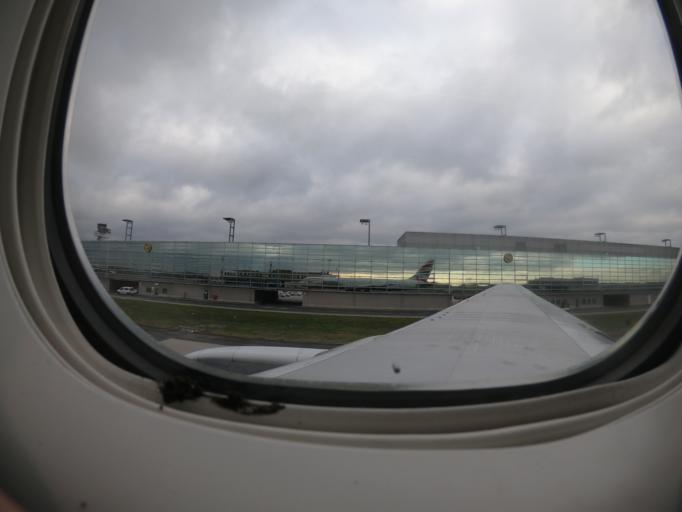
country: DE
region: Hesse
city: Kelsterbach
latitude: 50.0436
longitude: 8.5642
